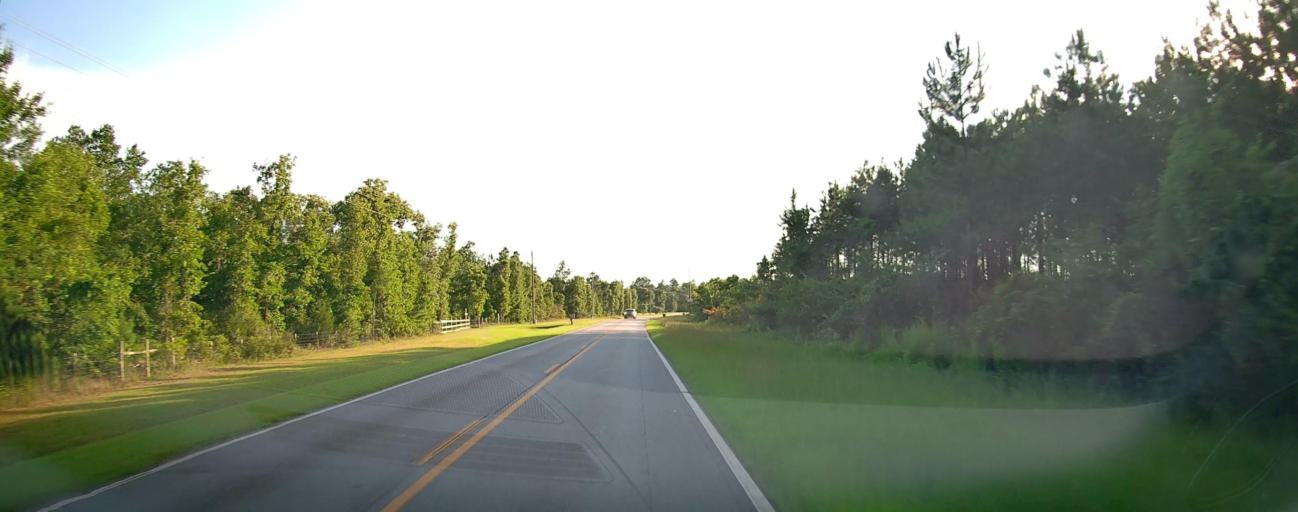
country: US
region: Georgia
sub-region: Peach County
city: Byron
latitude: 32.7085
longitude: -83.8001
